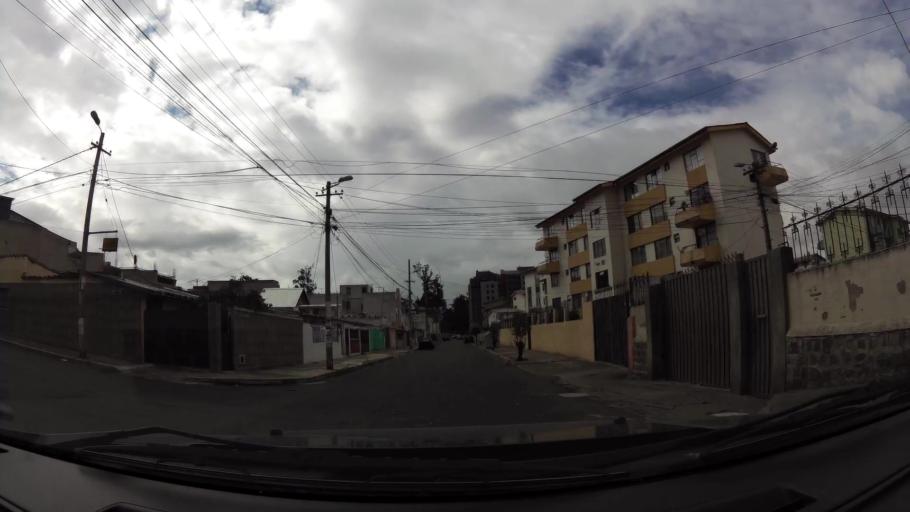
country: EC
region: Pichincha
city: Quito
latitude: -0.1362
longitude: -78.4988
